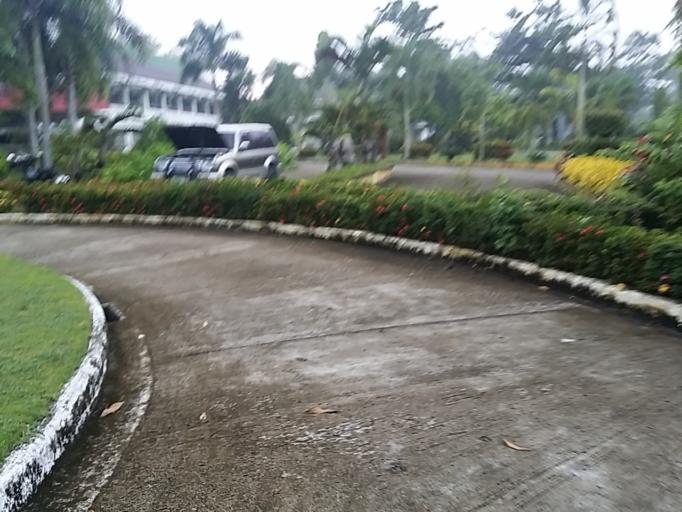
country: PH
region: Caraga
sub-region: Province of Agusan del Sur
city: Patin-ay
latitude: 8.5535
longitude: 125.9423
